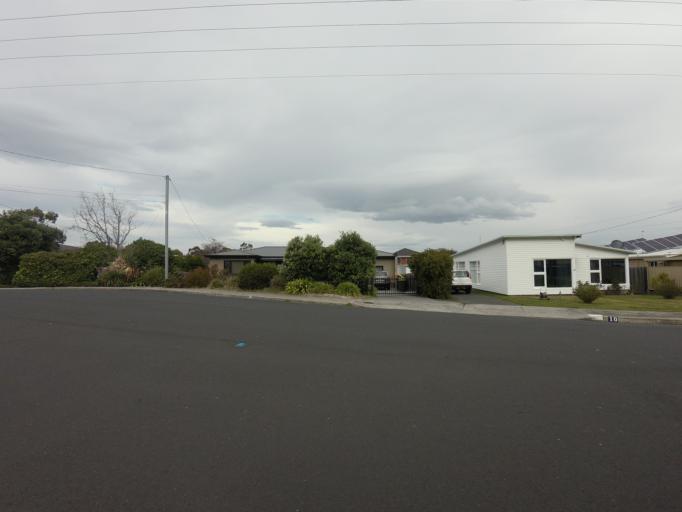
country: AU
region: Tasmania
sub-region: Clarence
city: Howrah
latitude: -42.8789
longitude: 147.3977
